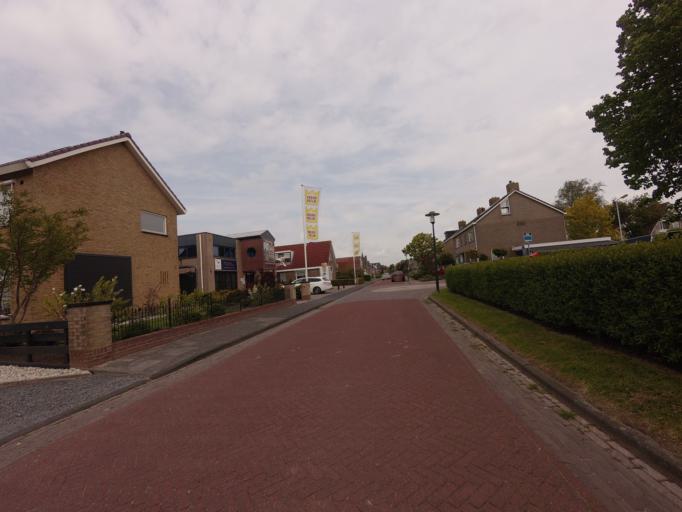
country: NL
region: Friesland
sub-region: Sudwest Fryslan
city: Bolsward
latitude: 53.0805
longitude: 5.4820
